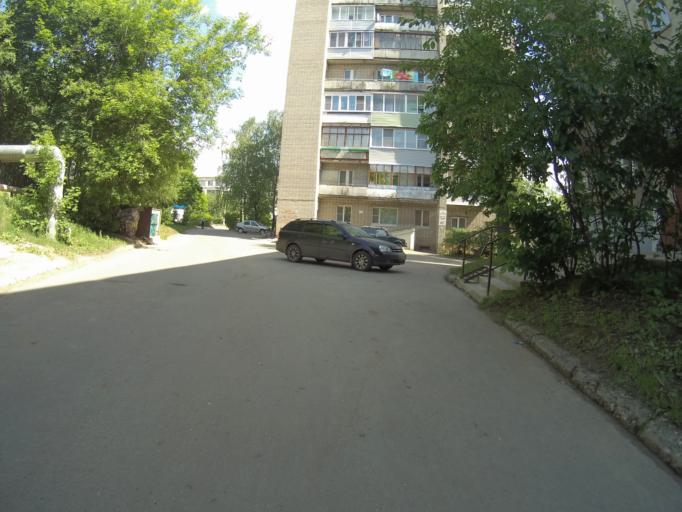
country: RU
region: Vladimir
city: Vladimir
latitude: 56.1286
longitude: 40.3537
